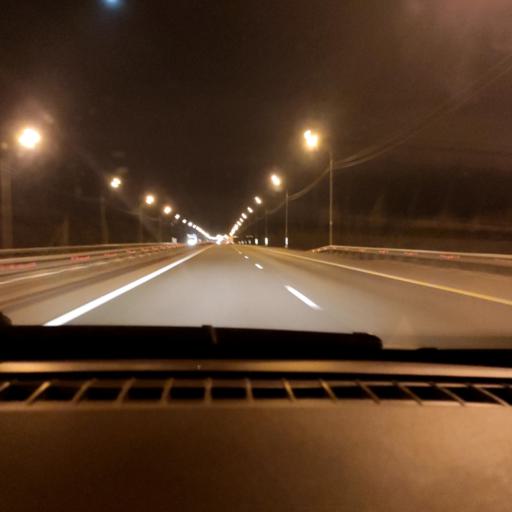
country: RU
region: Lipetsk
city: Khlevnoye
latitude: 52.2075
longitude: 39.1568
